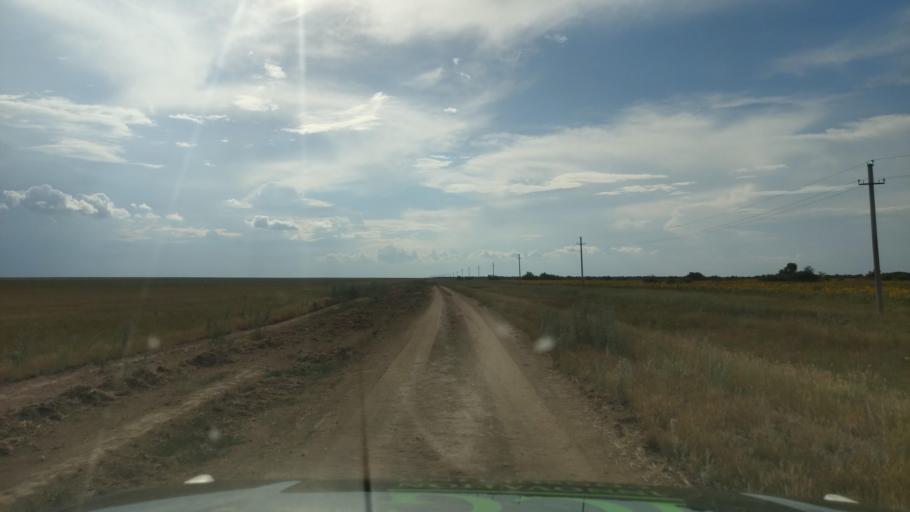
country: KZ
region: Pavlodar
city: Pavlodar
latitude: 52.5121
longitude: 77.5480
